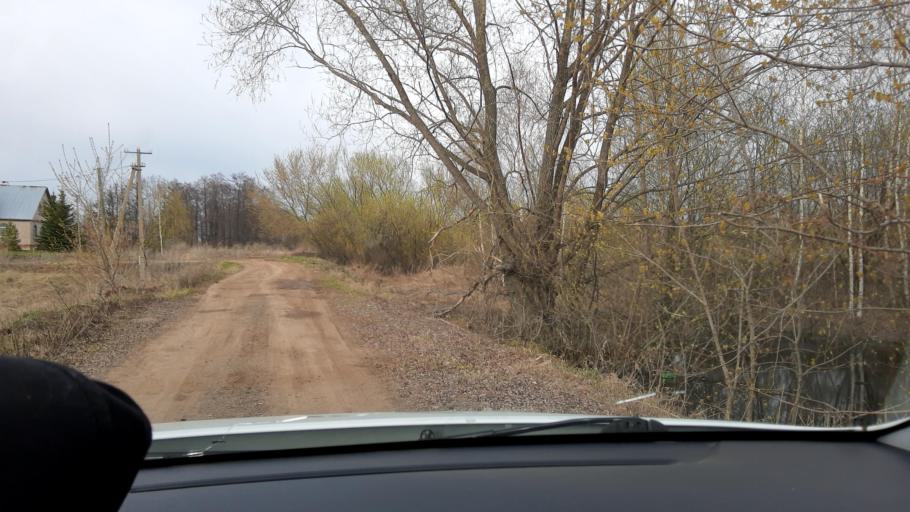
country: RU
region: Bashkortostan
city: Iglino
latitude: 54.8070
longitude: 56.4395
